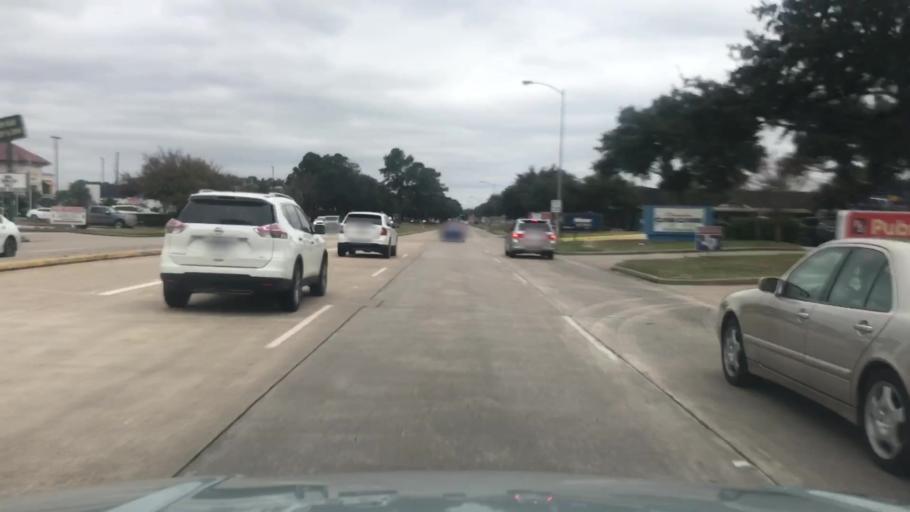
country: US
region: Texas
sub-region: Fort Bend County
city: Cinco Ranch
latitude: 29.7640
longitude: -95.7517
